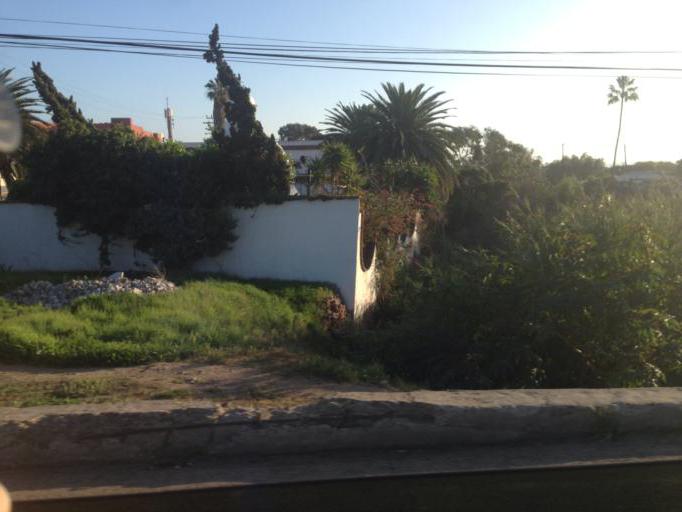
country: MX
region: Baja California
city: El Sauzal
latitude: 31.8668
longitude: -116.6632
